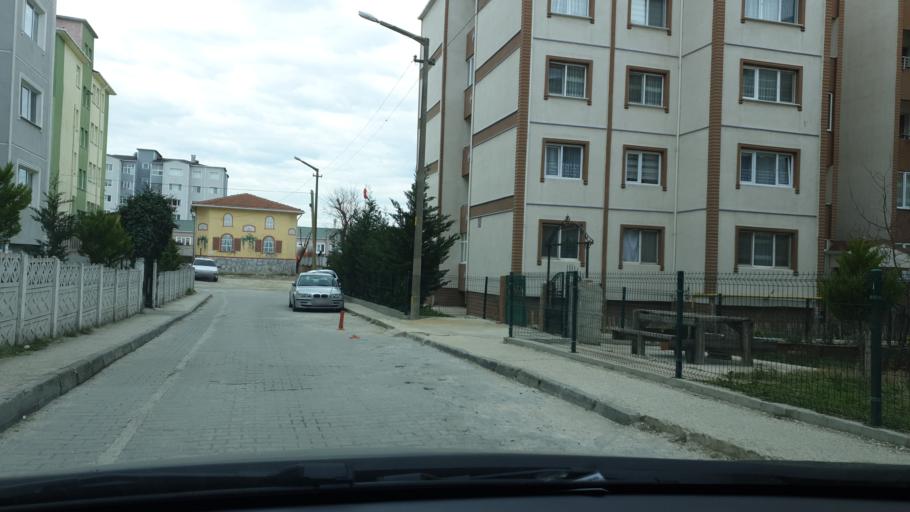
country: TR
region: Tekirdag
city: Cerkezkoey
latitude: 41.2847
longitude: 27.9817
